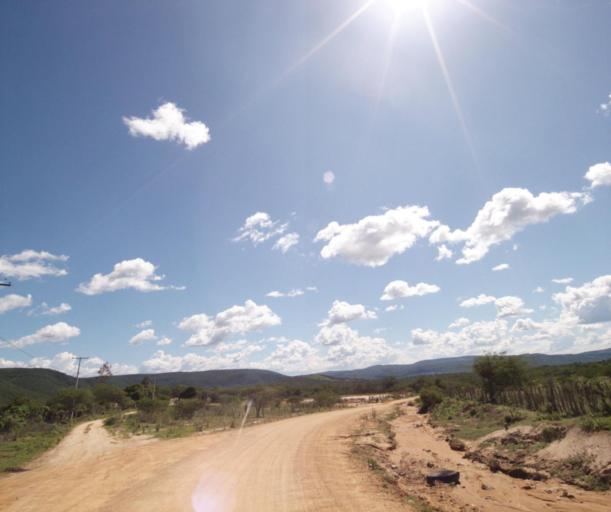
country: BR
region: Bahia
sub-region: Pocoes
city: Pocoes
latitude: -14.2565
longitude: -40.7145
